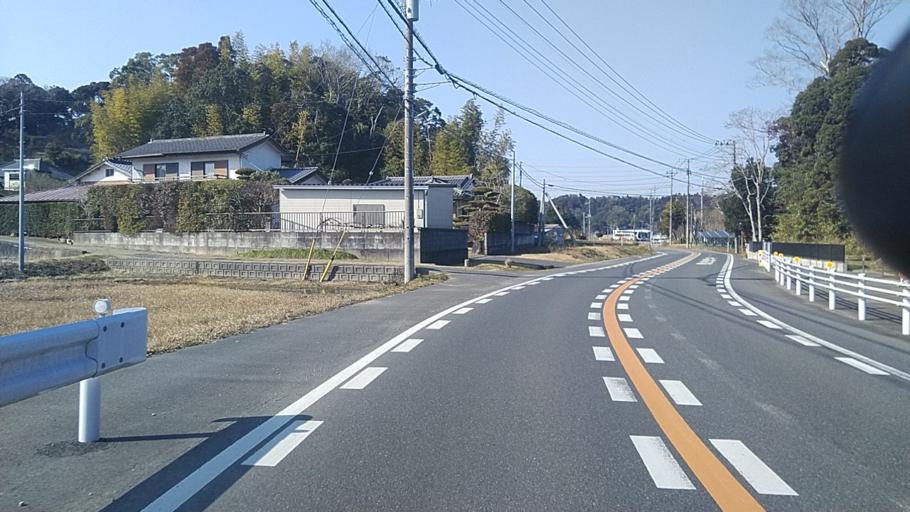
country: JP
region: Chiba
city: Mobara
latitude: 35.4613
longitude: 140.2845
